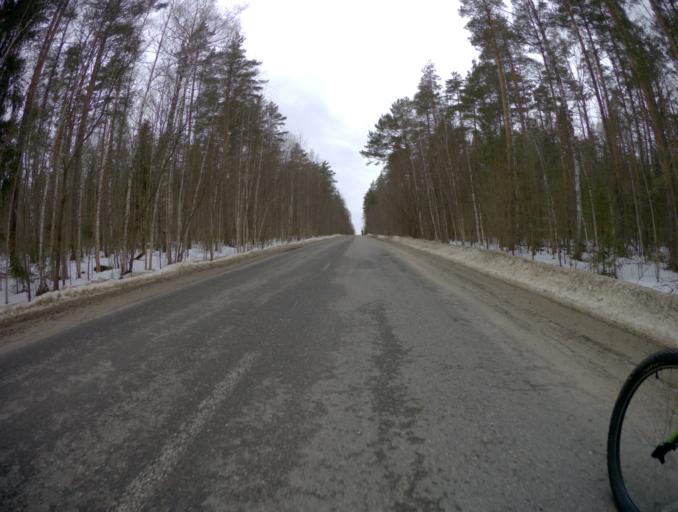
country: RU
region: Vladimir
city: Bogolyubovo
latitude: 56.1540
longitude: 40.5574
